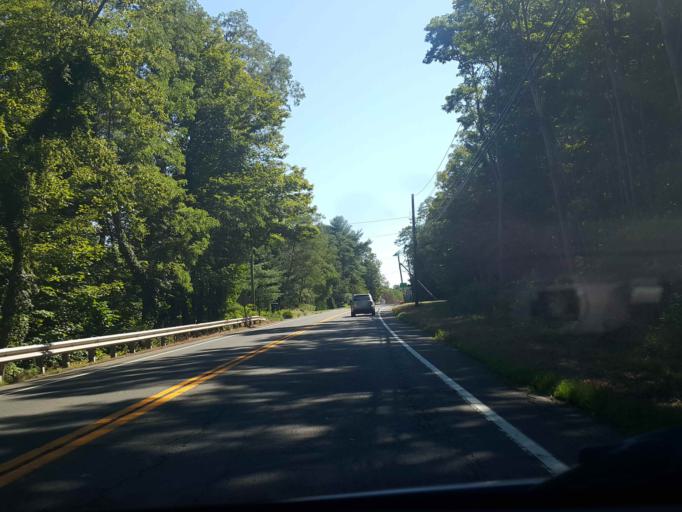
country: US
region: Connecticut
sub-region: New Haven County
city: North Branford
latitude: 41.3444
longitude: -72.7446
